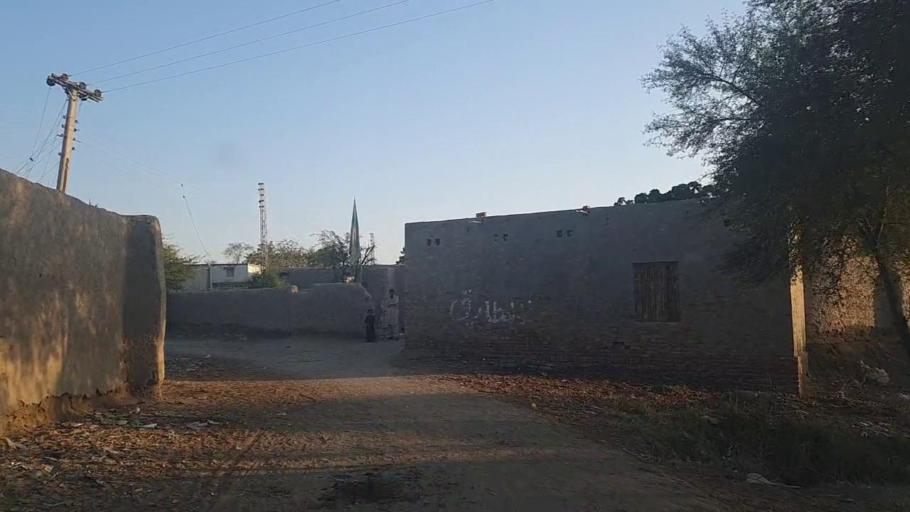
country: PK
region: Sindh
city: Jam Sahib
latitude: 26.3213
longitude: 68.7021
